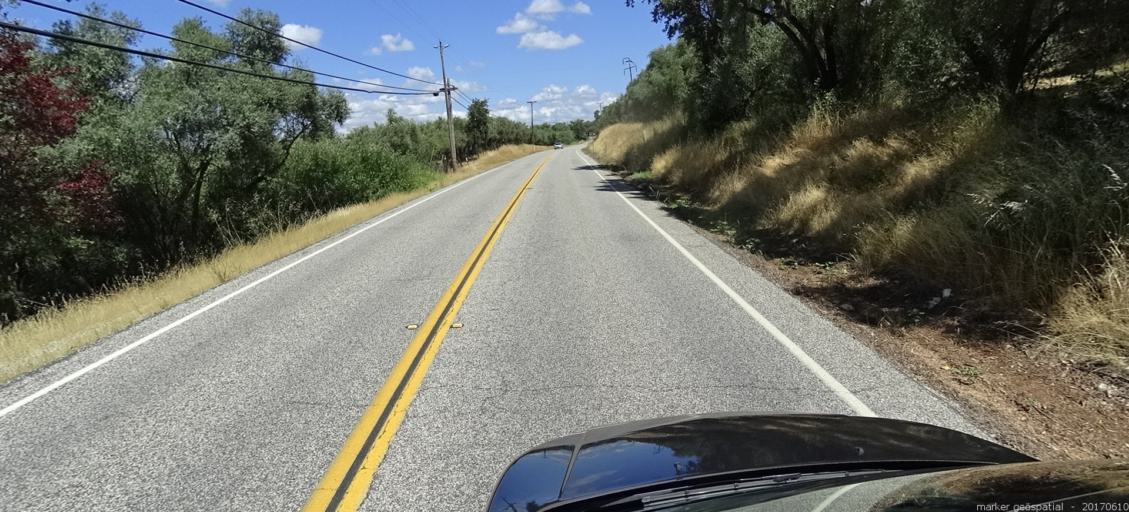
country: US
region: California
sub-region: Butte County
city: Oroville East
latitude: 39.4880
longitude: -121.4570
